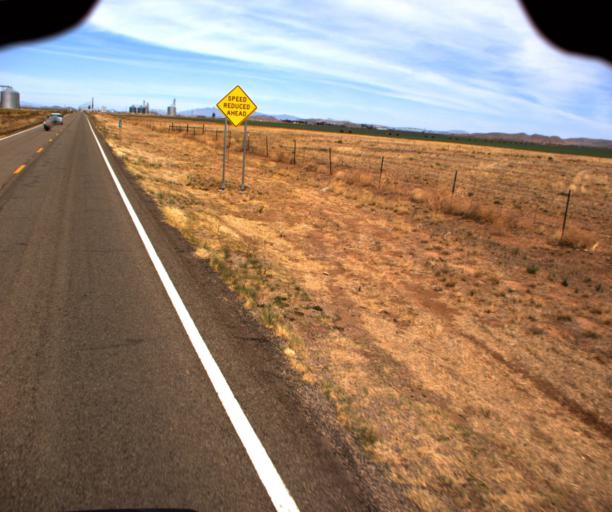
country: US
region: Arizona
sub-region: Cochise County
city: Tombstone
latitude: 31.7505
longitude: -109.6888
